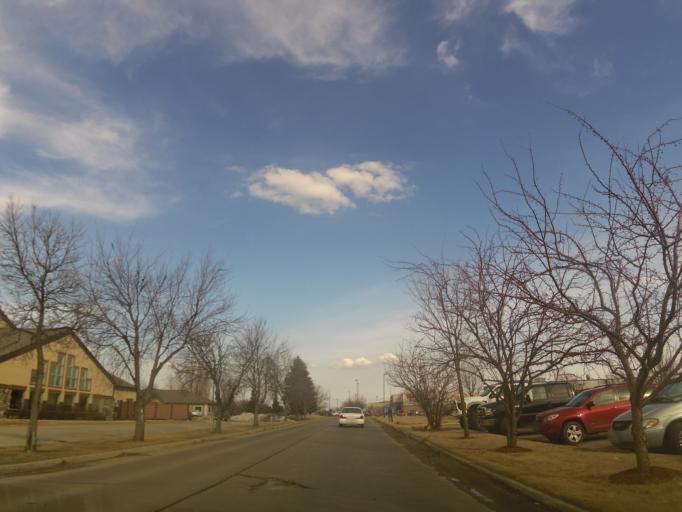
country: US
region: North Dakota
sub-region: Grand Forks County
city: Grand Forks
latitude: 47.8880
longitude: -97.0729
